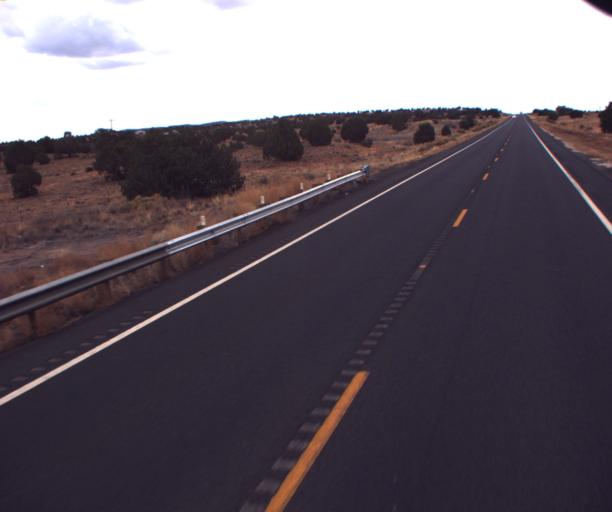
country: US
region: Arizona
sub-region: Coconino County
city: Kaibito
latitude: 36.4544
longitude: -110.7083
